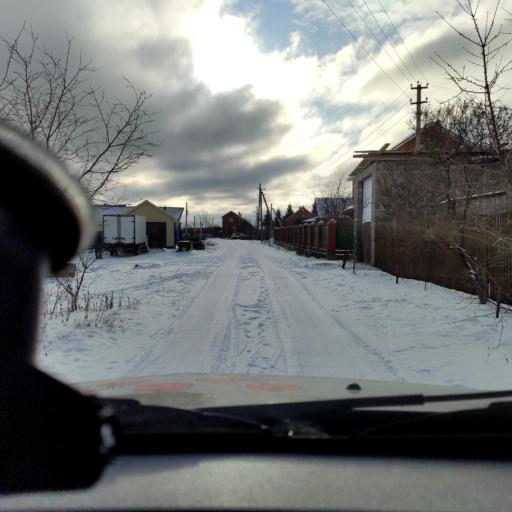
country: RU
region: Bashkortostan
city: Avdon
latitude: 54.7863
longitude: 55.7209
